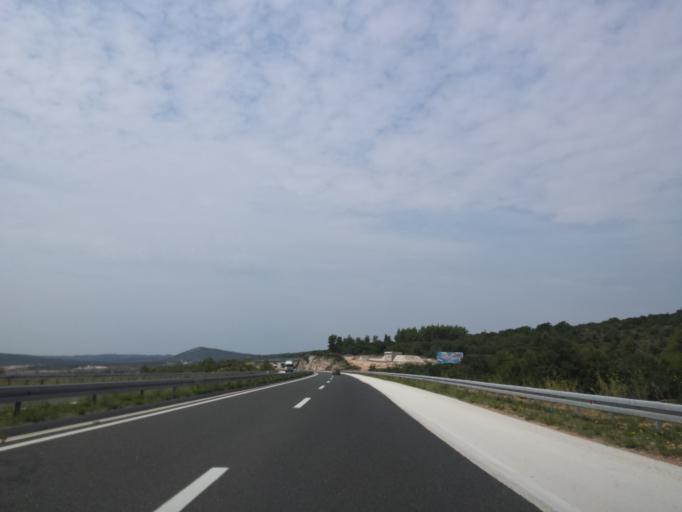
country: HR
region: Zadarska
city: Posedarje
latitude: 44.2185
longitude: 15.4758
